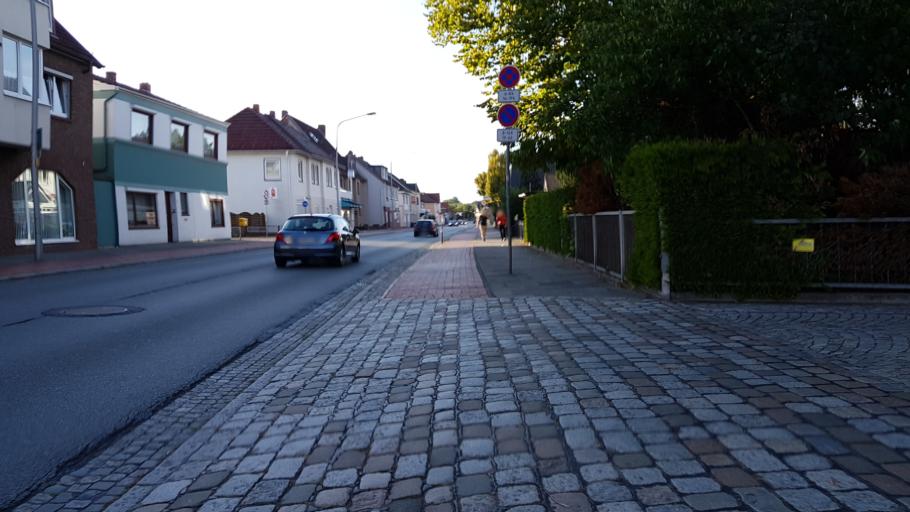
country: DE
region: Lower Saxony
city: Oyten
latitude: 53.0354
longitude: 8.9500
